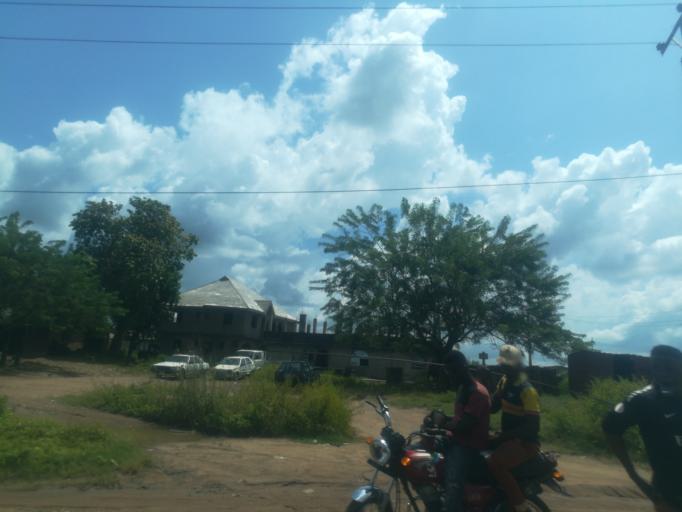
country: NG
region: Oyo
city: Lalupon
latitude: 7.4414
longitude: 4.0084
